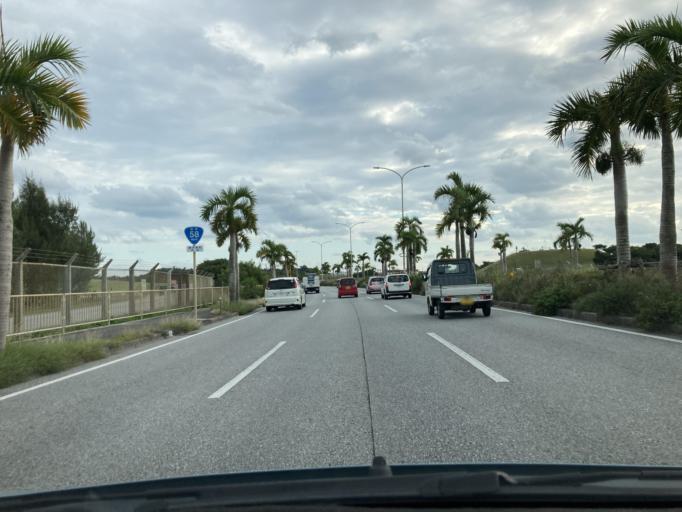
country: JP
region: Okinawa
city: Chatan
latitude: 26.3476
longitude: 127.7471
